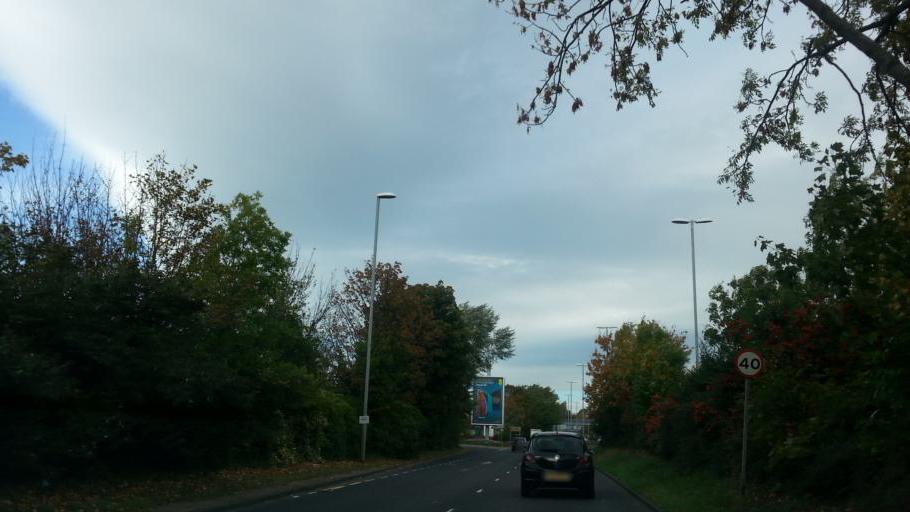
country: GB
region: England
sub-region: City and Borough of Leeds
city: Leeds
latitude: 53.7883
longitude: -1.5669
